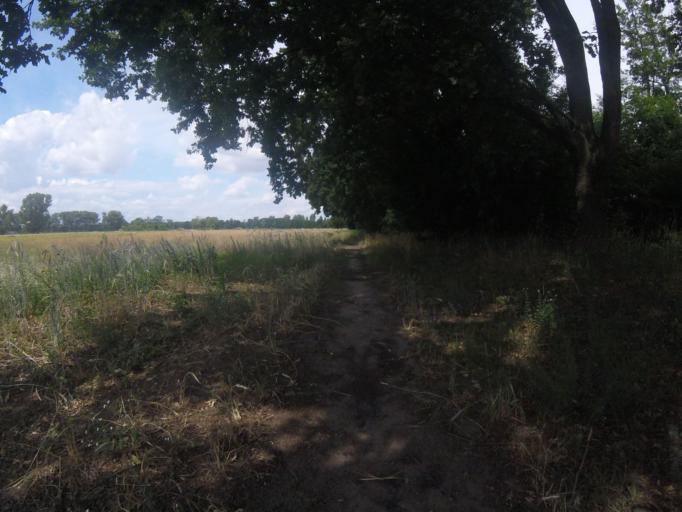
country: DE
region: Brandenburg
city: Konigs Wusterhausen
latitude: 52.2849
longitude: 13.6072
